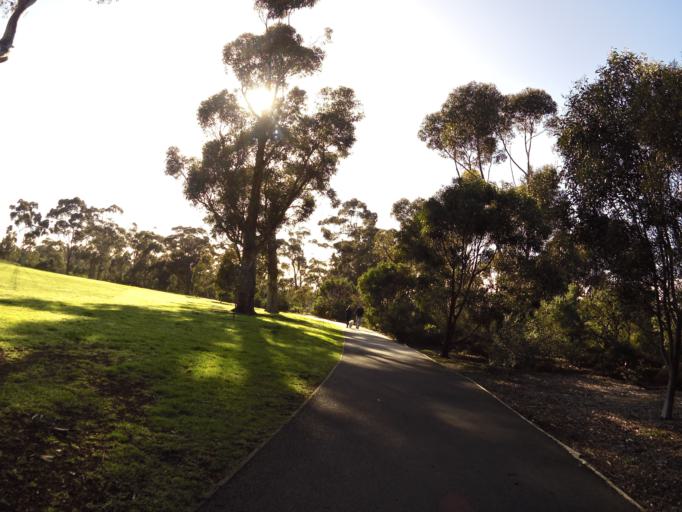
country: AU
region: Victoria
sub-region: Stonnington
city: Toorak
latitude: -37.8271
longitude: 145.0140
